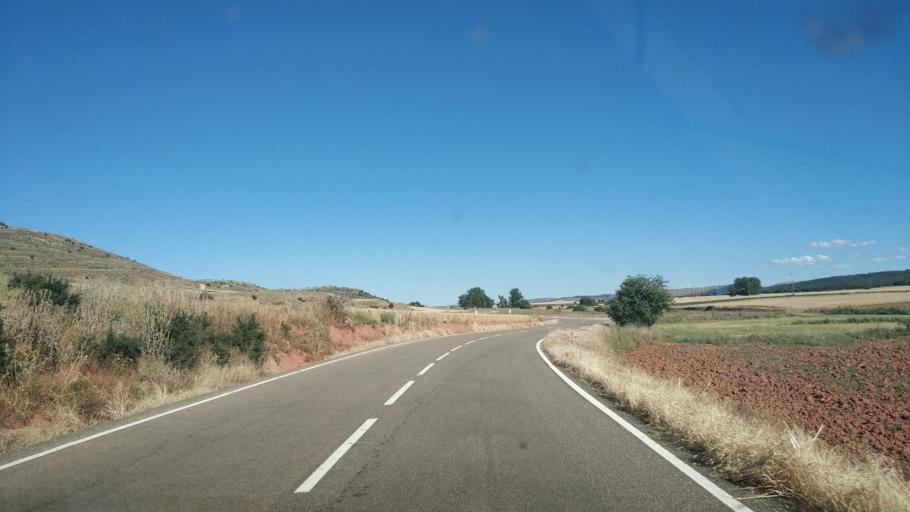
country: ES
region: Castille and Leon
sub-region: Provincia de Soria
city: Montejo de Tiermes
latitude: 41.3651
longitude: -3.1908
